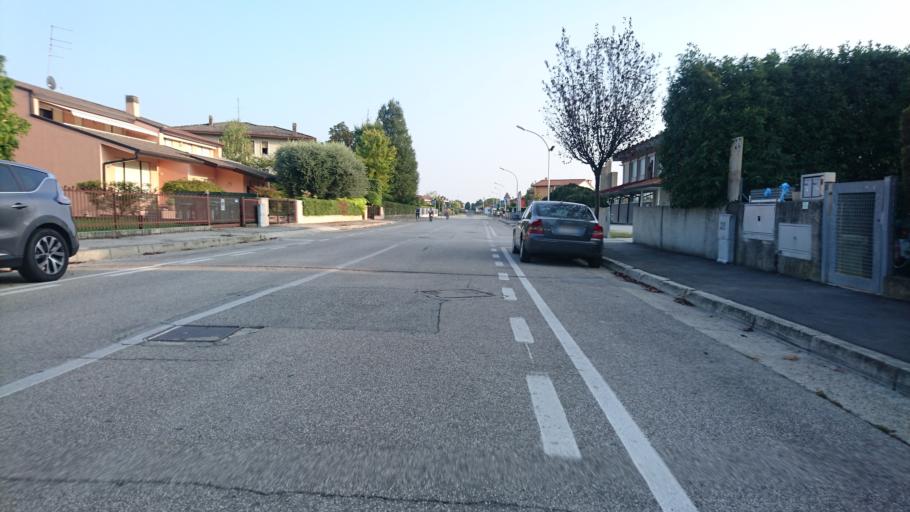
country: IT
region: Veneto
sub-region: Provincia di Padova
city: Limena
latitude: 45.4722
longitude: 11.8431
